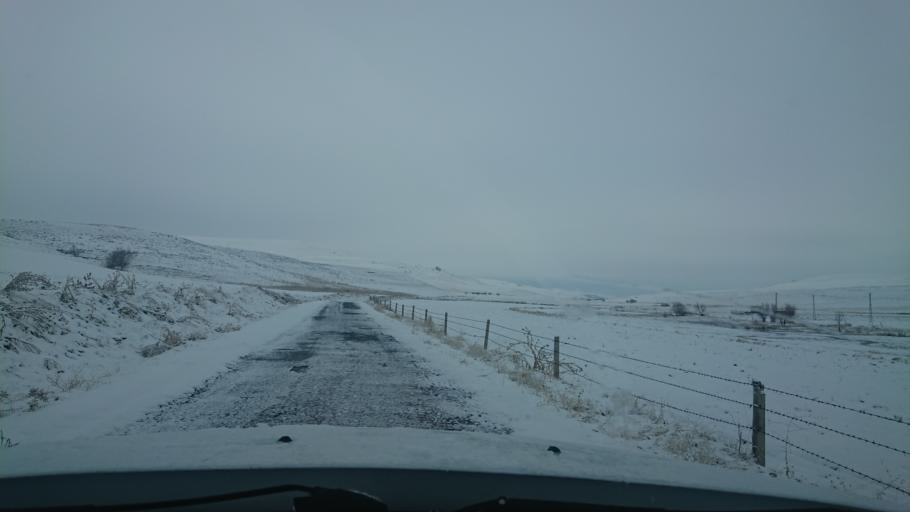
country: TR
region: Aksaray
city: Acipinar
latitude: 38.6805
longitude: 33.8648
